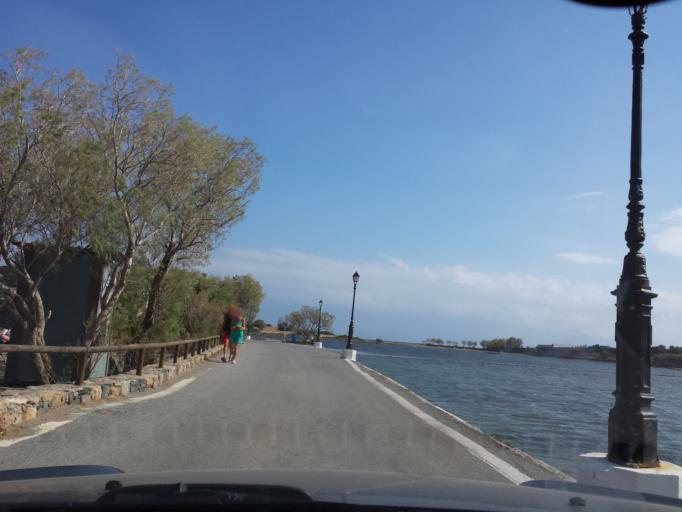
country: GR
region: Crete
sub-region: Nomos Lasithiou
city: Skhisma
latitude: 35.2576
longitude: 25.7310
